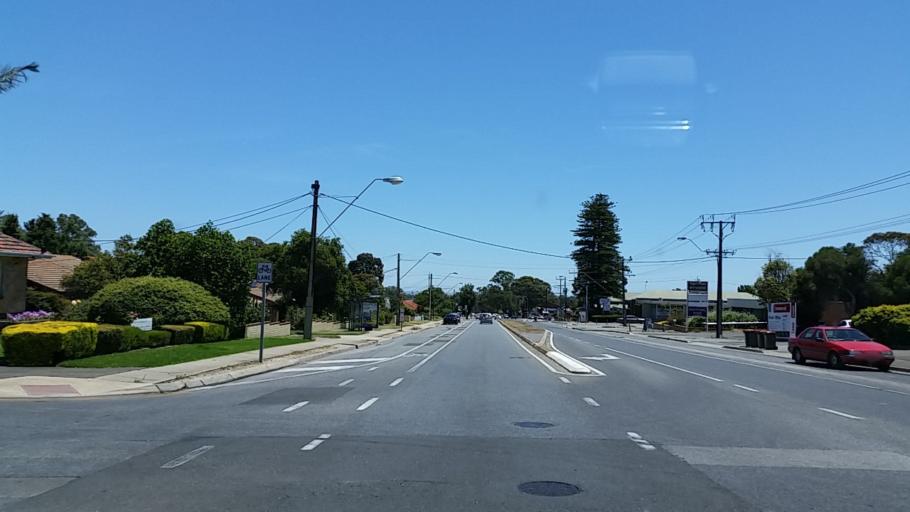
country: AU
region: South Australia
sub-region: Tea Tree Gully
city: Hope Valley
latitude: -34.8208
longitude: 138.7219
